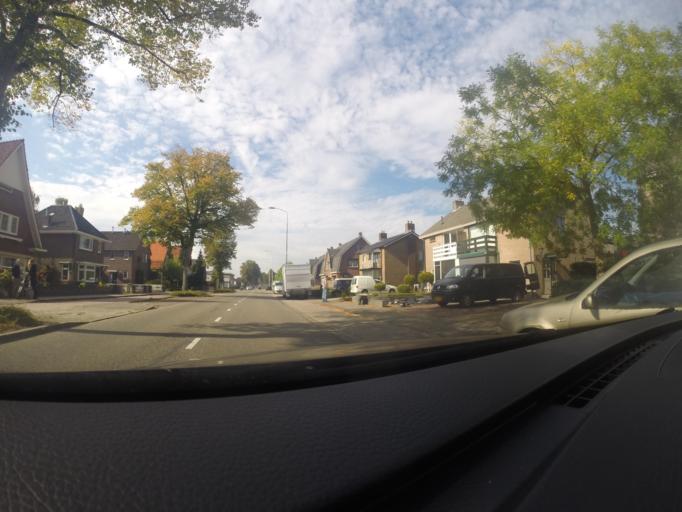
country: NL
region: Gelderland
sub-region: Oude IJsselstreek
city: Gendringen
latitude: 51.9261
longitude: 6.3551
